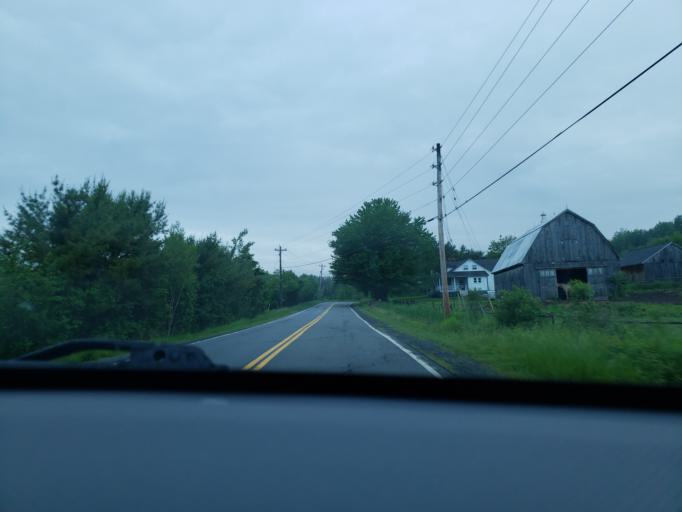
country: CA
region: Nova Scotia
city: Windsor
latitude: 45.0610
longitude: -63.9807
